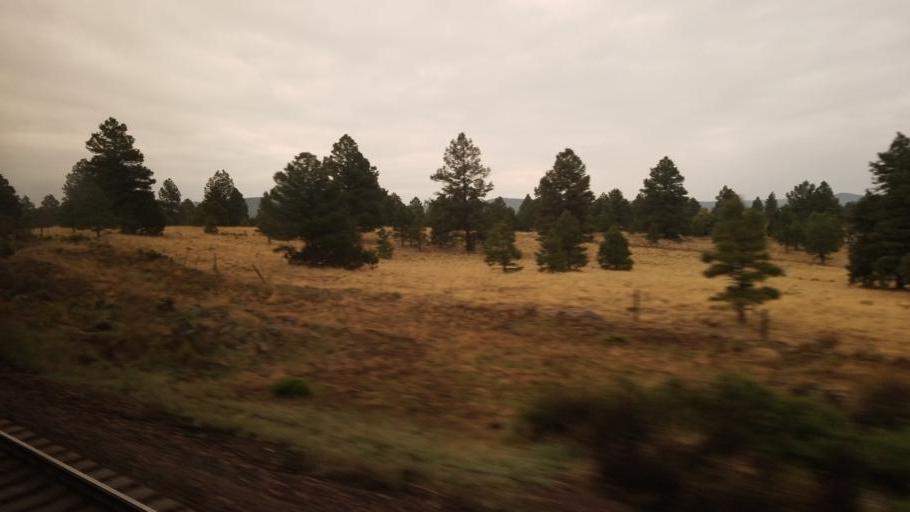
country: US
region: Arizona
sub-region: Coconino County
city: Parks
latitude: 35.2402
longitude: -111.9792
